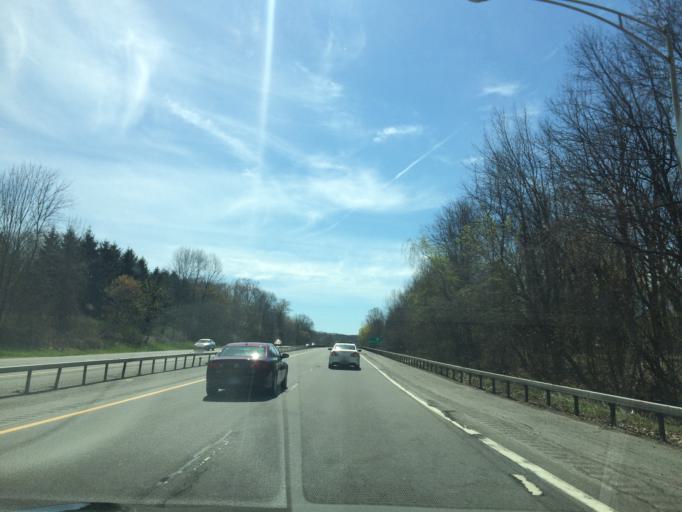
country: US
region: New York
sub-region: Monroe County
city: East Rochester
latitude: 43.0749
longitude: -77.4818
